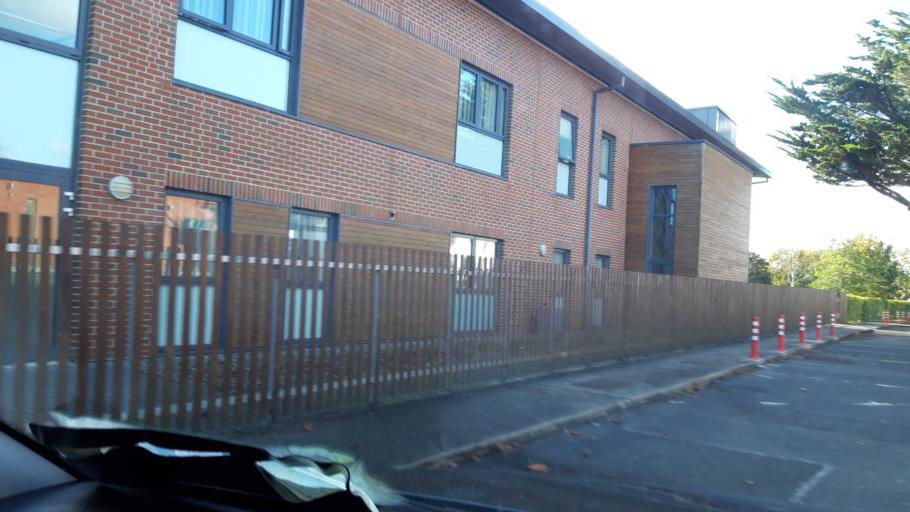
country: IE
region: Leinster
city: Raheny
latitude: 53.3824
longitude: -6.1807
